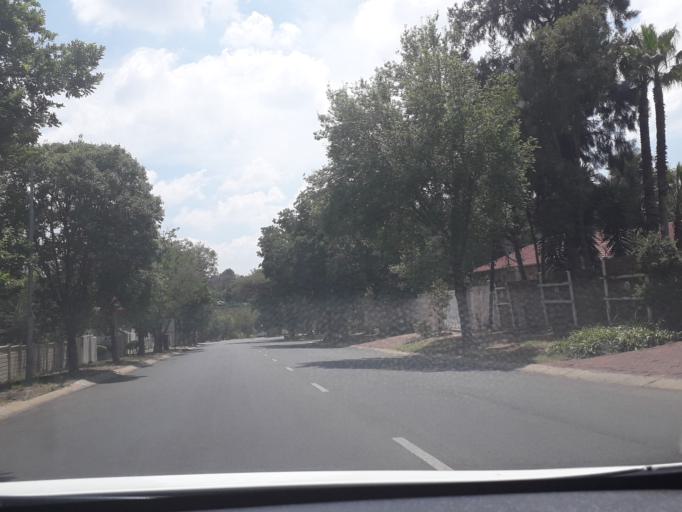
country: ZA
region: Gauteng
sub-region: City of Johannesburg Metropolitan Municipality
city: Midrand
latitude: -26.0379
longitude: 28.0711
